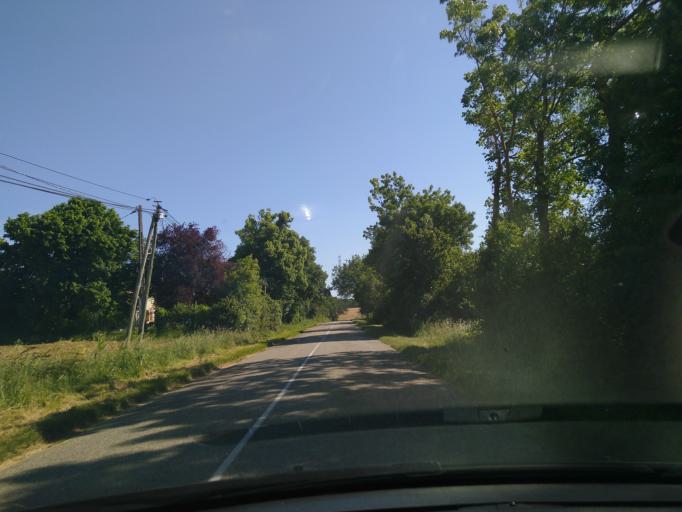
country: FR
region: Midi-Pyrenees
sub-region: Departement du Gers
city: Aubiet
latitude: 43.5614
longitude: 0.7979
